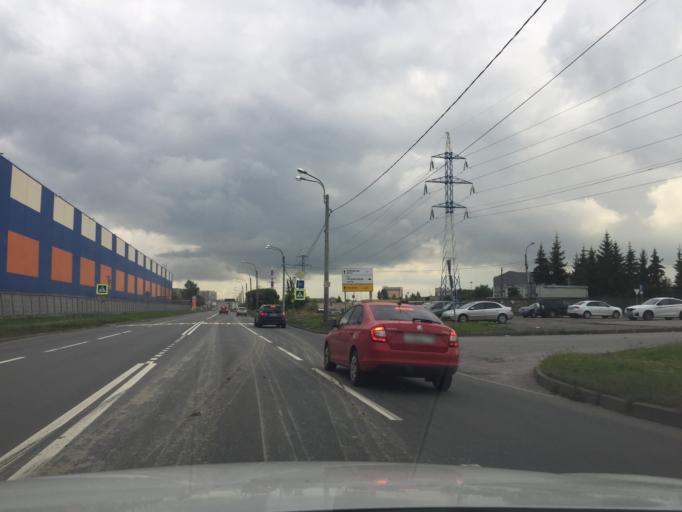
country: RU
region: St.-Petersburg
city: Dachnoye
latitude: 59.8402
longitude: 30.3002
